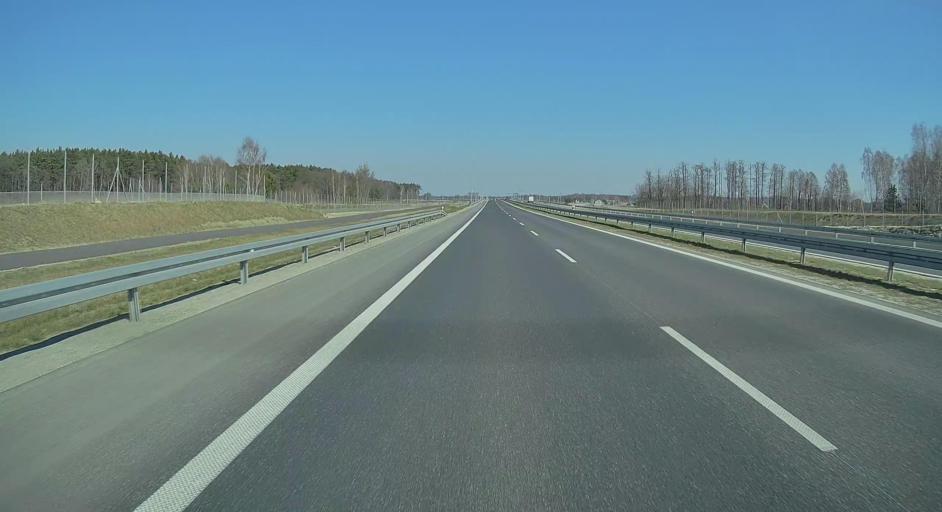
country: PL
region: Subcarpathian Voivodeship
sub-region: Powiat lezajski
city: Letownia
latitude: 50.3265
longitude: 22.1858
